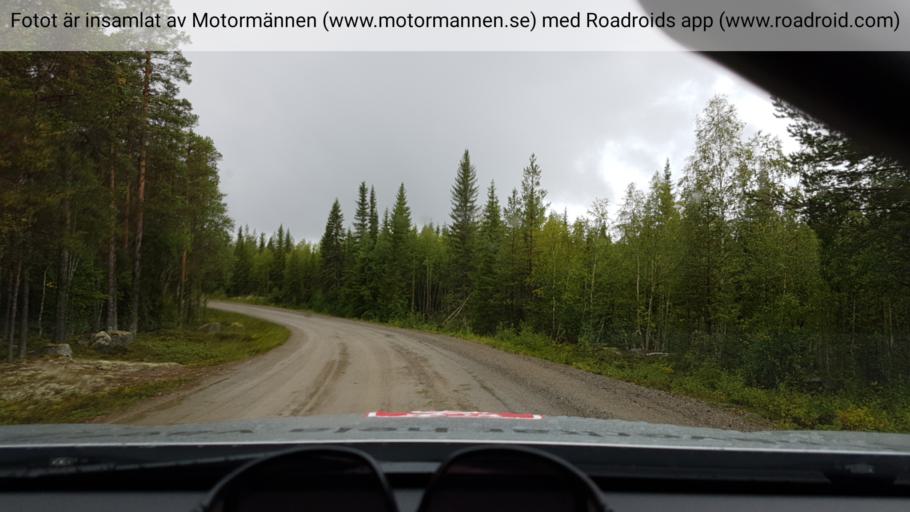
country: SE
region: Vaesterbotten
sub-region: Storumans Kommun
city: Storuman
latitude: 64.9505
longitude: 17.5259
